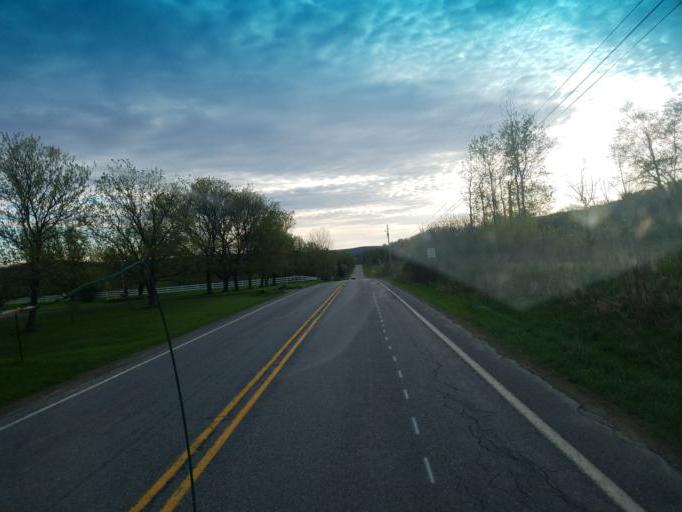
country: US
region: Pennsylvania
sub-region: Tioga County
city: Westfield
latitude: 41.9301
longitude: -77.7248
